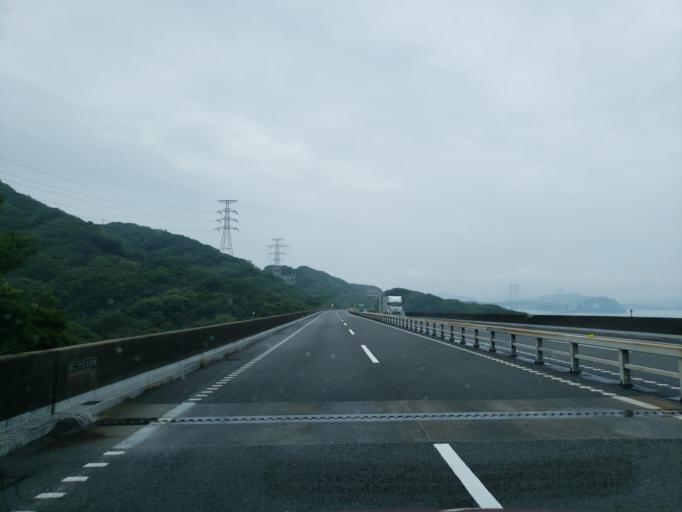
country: JP
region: Hyogo
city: Fukura
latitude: 34.2548
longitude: 134.6779
